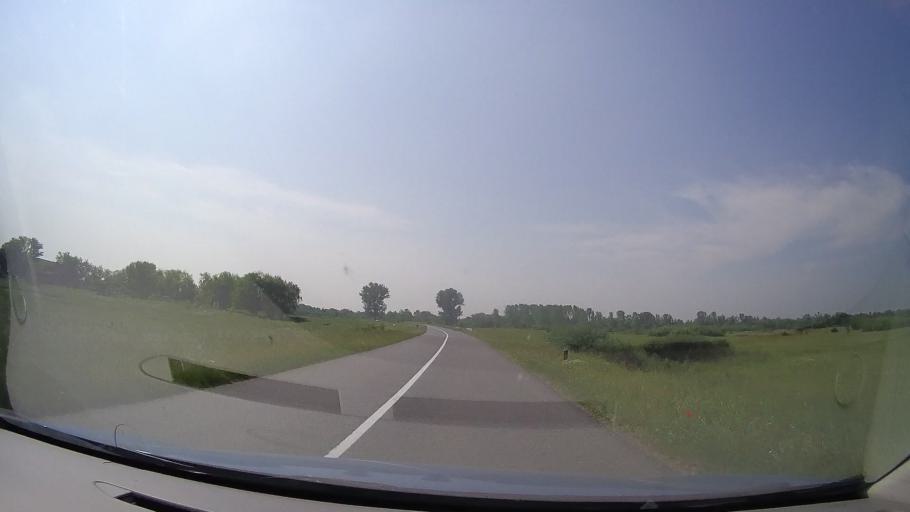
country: RS
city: Jarkovac
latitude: 45.2786
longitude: 20.7626
